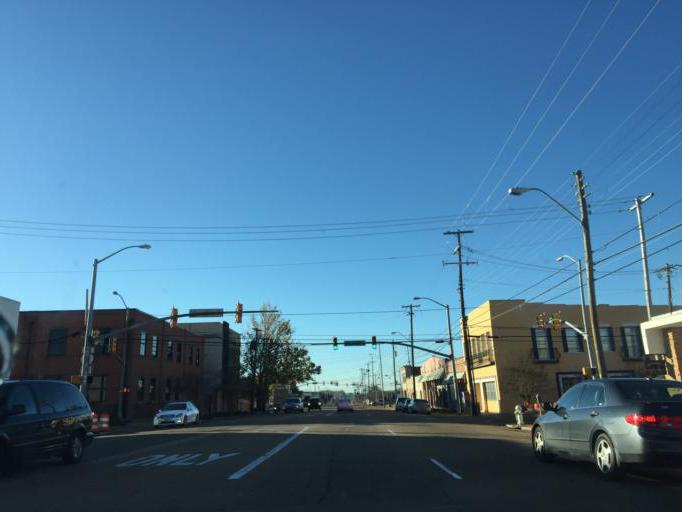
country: US
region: Mississippi
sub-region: Hinds County
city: Jackson
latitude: 32.2964
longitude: -90.1809
